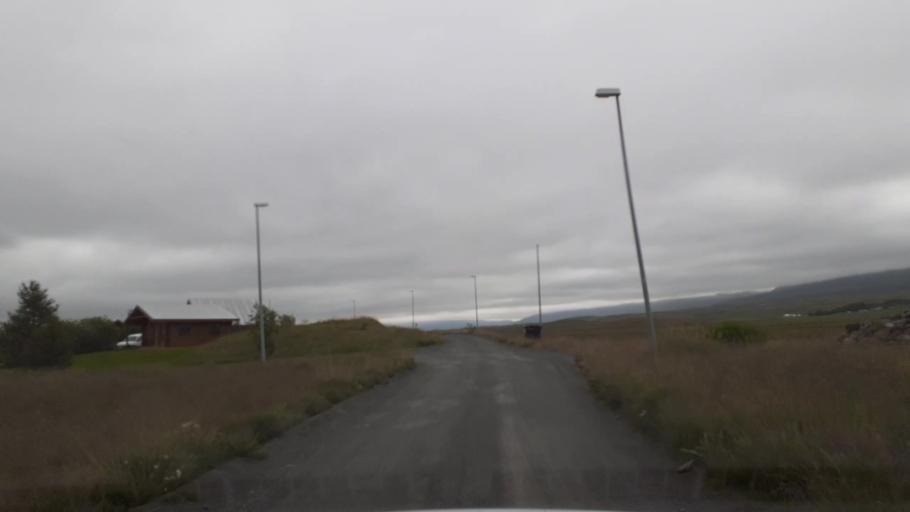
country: IS
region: Northwest
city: Saudarkrokur
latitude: 65.5497
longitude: -19.4556
